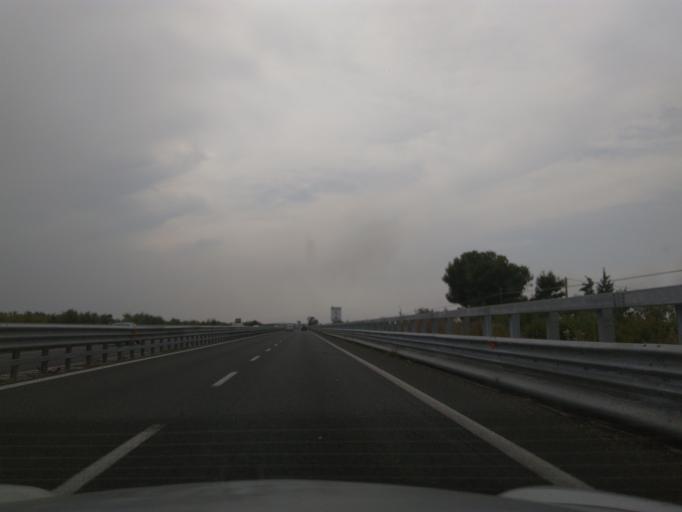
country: IT
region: Apulia
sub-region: Provincia di Bari
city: Giovinazzo
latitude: 41.1701
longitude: 16.6978
